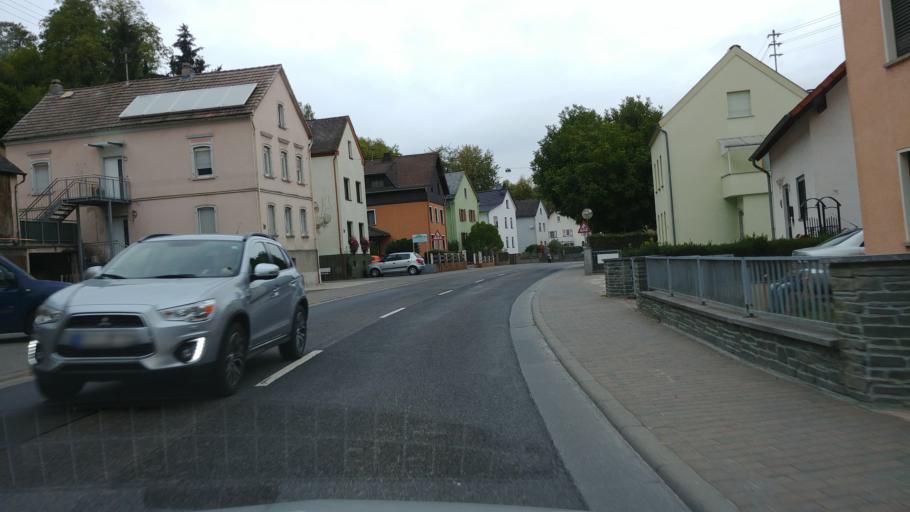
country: DE
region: Rheinland-Pfalz
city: Niederneisen
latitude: 50.3318
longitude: 8.0567
